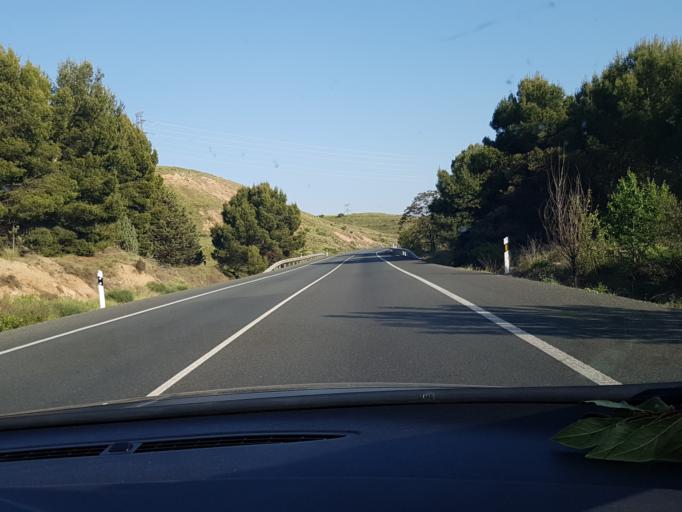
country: ES
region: La Rioja
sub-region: Provincia de La Rioja
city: Arrubal
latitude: 42.4089
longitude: -2.2533
